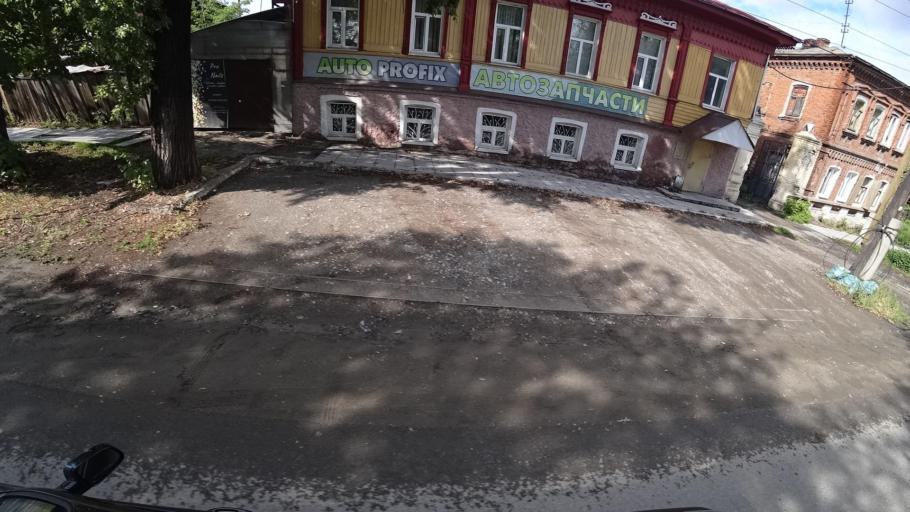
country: RU
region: Sverdlovsk
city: Kamyshlov
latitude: 56.8476
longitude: 62.7030
